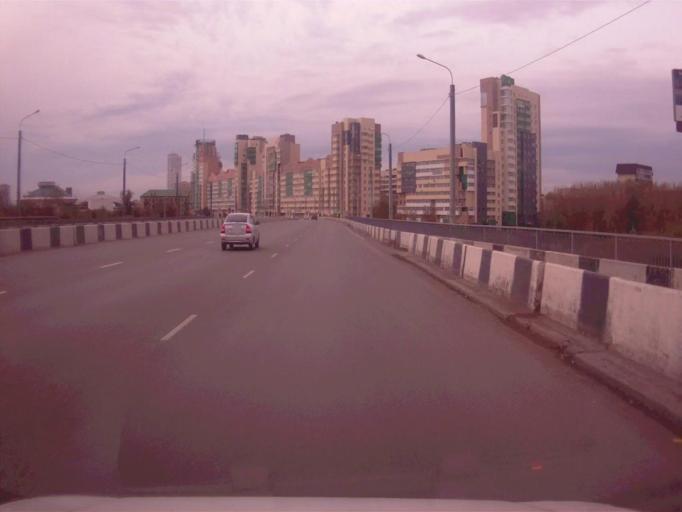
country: RU
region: Chelyabinsk
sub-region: Gorod Chelyabinsk
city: Chelyabinsk
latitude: 55.1728
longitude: 61.4096
